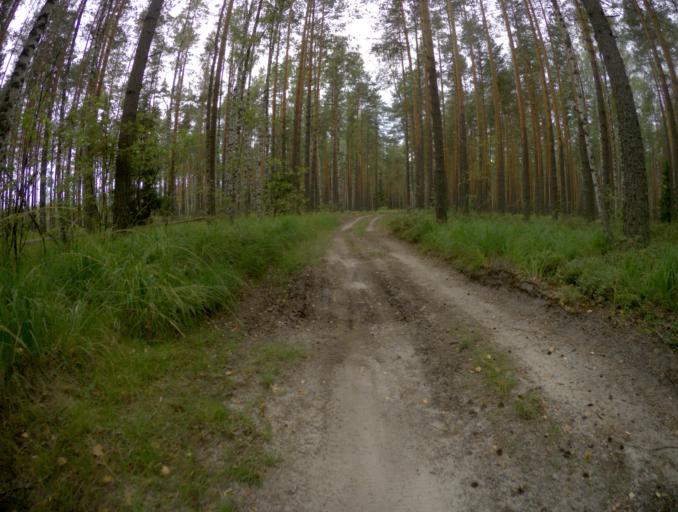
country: RU
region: Vladimir
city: Ivanishchi
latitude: 55.8434
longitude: 40.3326
